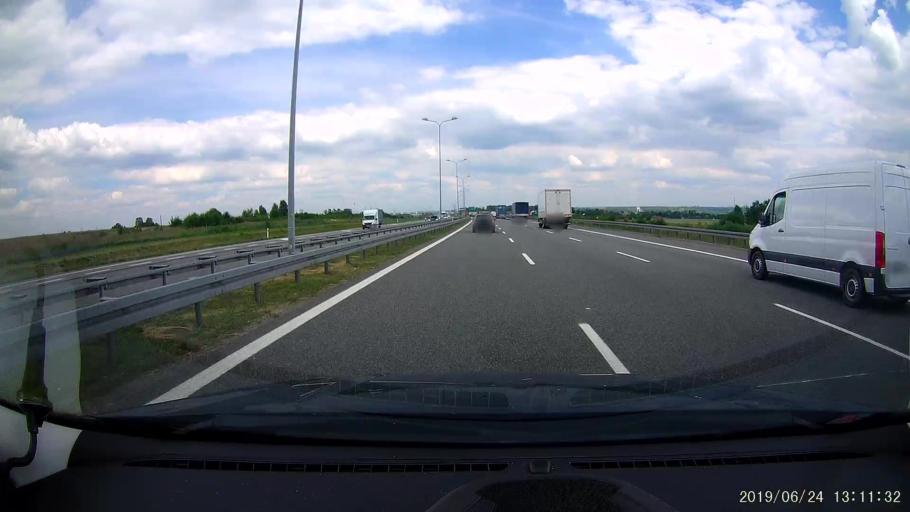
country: PL
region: Silesian Voivodeship
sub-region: Powiat gliwicki
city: Gieraltowice
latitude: 50.2445
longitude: 18.7127
